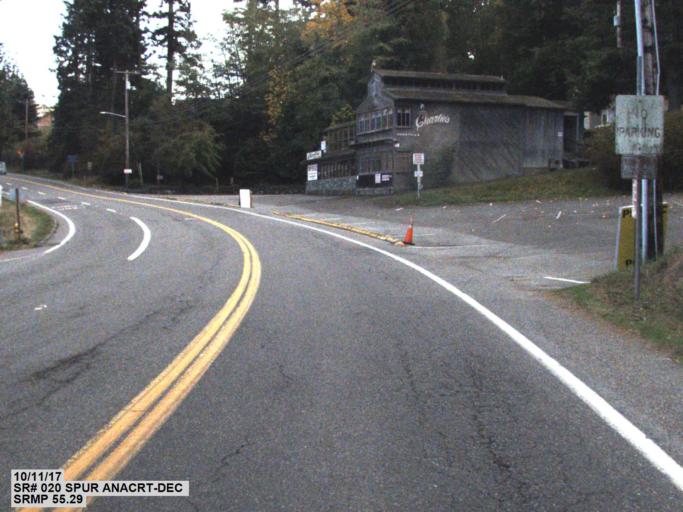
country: US
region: Washington
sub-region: Jefferson County
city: Port Hadlock-Irondale
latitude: 48.0659
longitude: -122.8198
